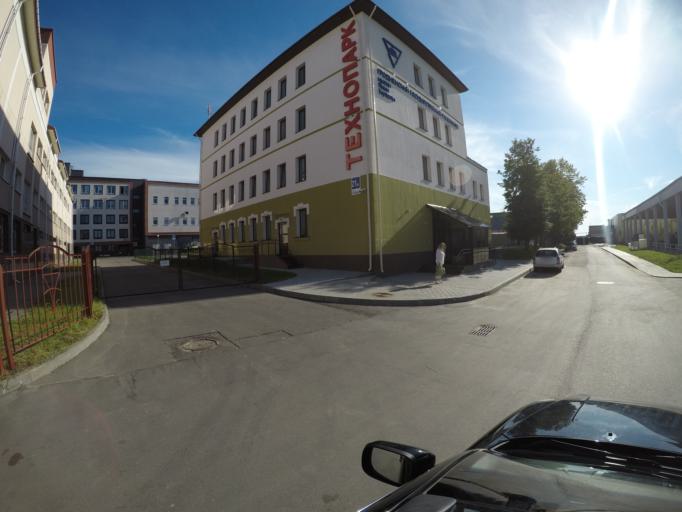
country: BY
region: Grodnenskaya
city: Hrodna
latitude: 53.7114
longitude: 23.8258
